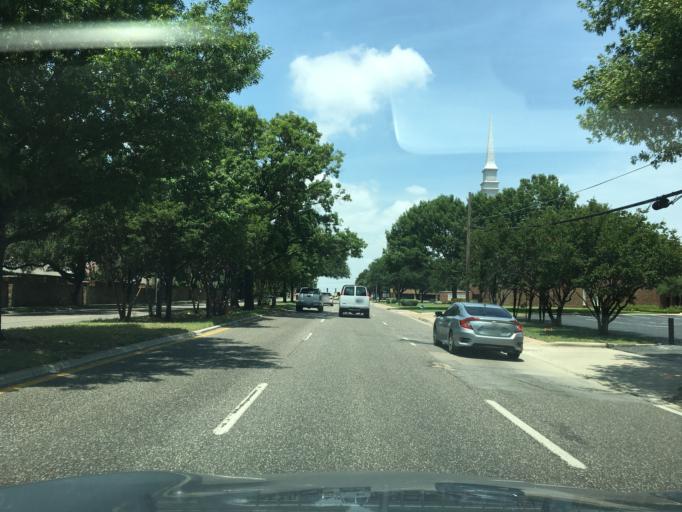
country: US
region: Texas
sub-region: Dallas County
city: Addison
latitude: 32.9200
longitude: -96.8035
